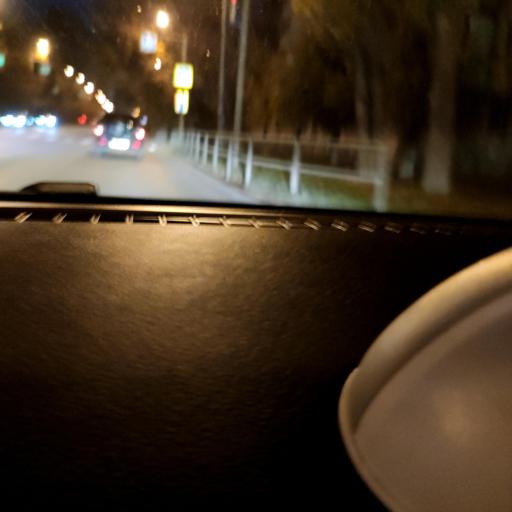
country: RU
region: Samara
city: Petra-Dubrava
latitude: 53.2233
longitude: 50.2761
